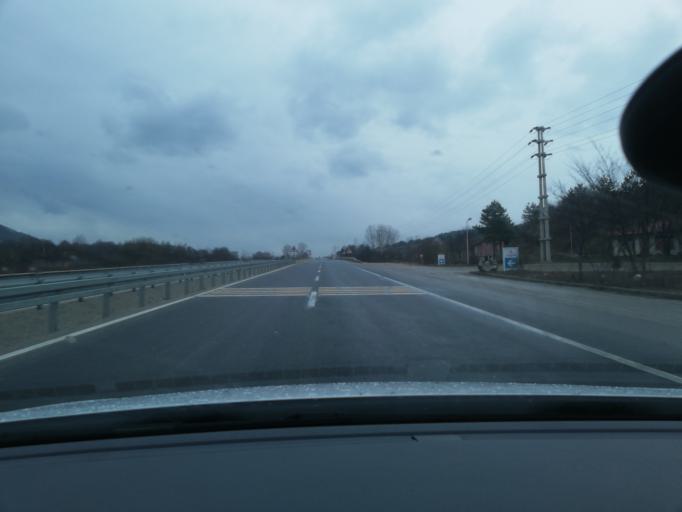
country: TR
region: Bolu
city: Yenicaga
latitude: 40.7587
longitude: 31.9328
